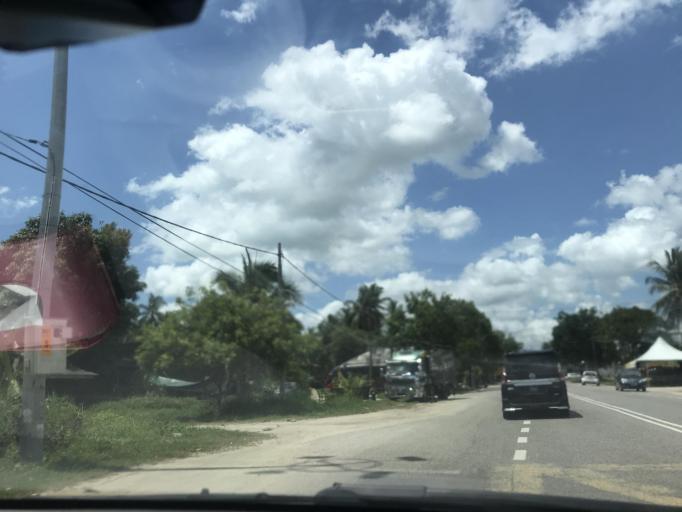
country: TH
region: Narathiwat
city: Tak Bai
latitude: 6.2270
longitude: 102.0966
